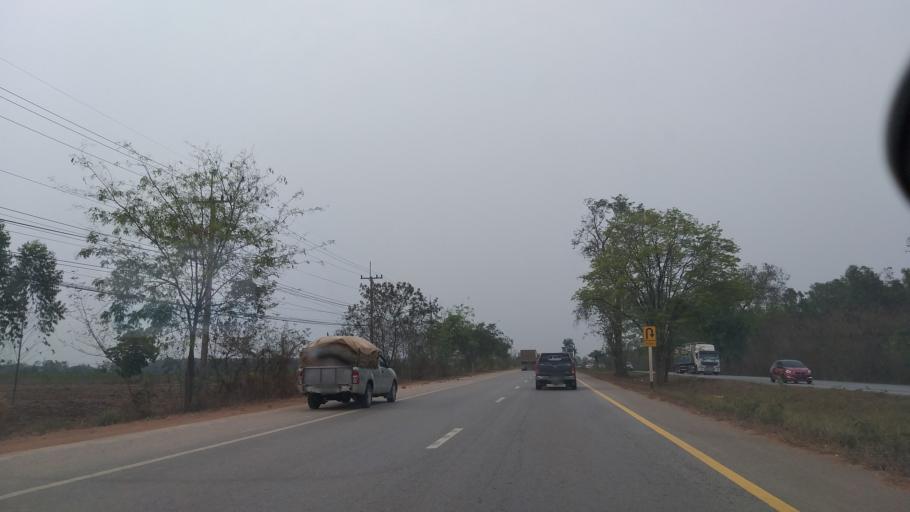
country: TH
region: Chachoengsao
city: Plaeng Yao
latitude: 13.5346
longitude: 101.2629
